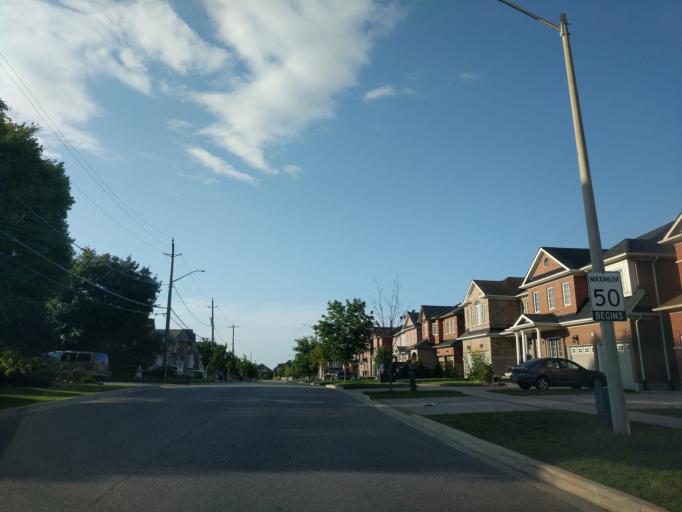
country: CA
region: Ontario
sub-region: York
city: Richmond Hill
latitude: 43.9056
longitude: -79.4546
